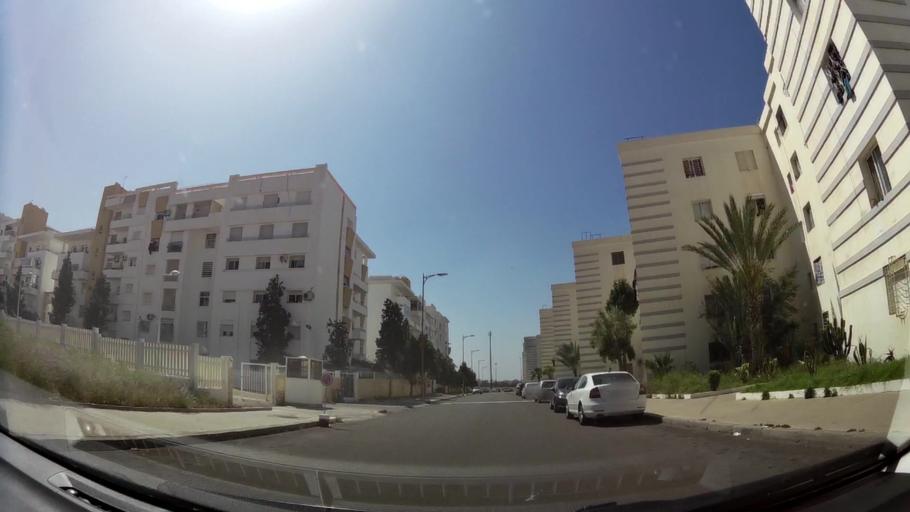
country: MA
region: Souss-Massa-Draa
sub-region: Agadir-Ida-ou-Tnan
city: Agadir
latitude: 30.4359
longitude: -9.5725
